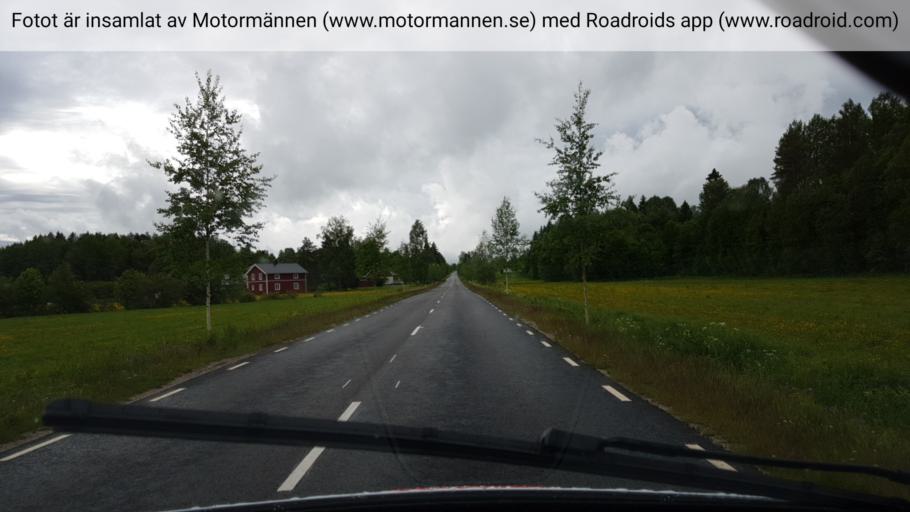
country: SE
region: Vaesterbotten
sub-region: Vannas Kommun
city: Vannasby
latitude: 63.8820
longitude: 19.8895
